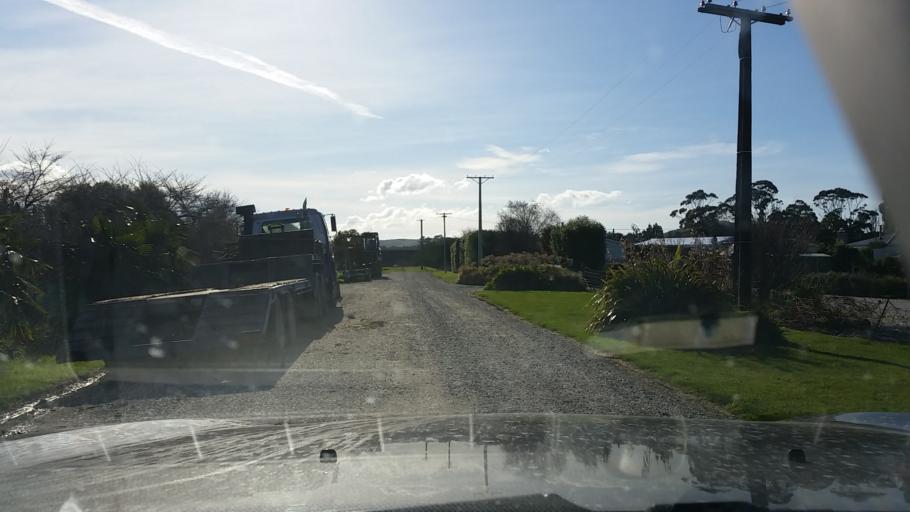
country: NZ
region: Marlborough
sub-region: Marlborough District
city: Blenheim
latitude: -41.8279
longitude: 174.1397
